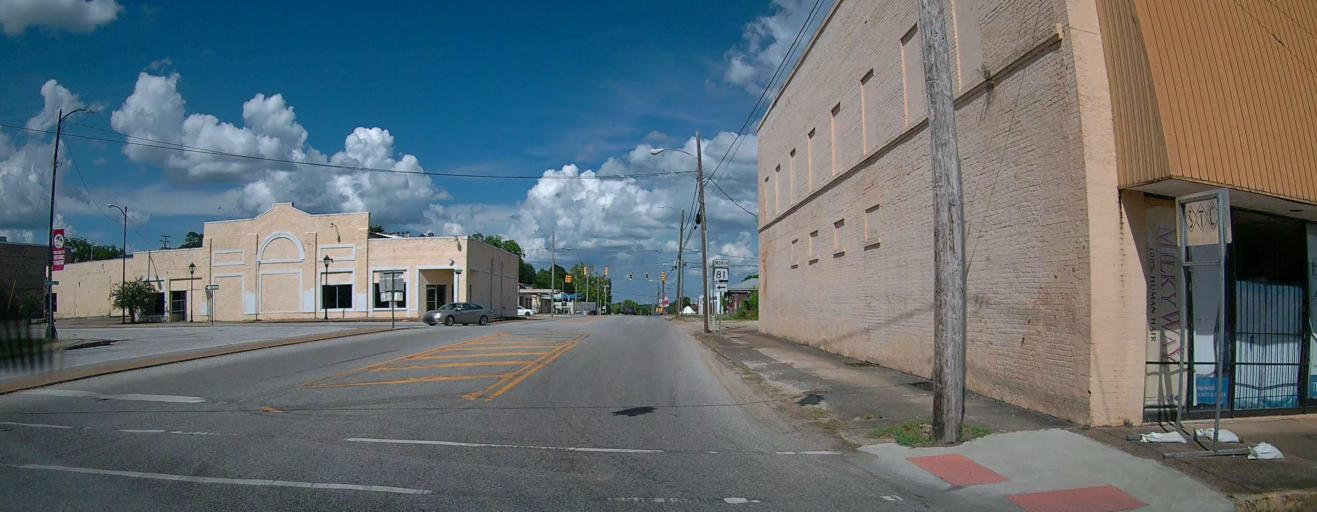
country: US
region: Alabama
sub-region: Macon County
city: Tuskegee
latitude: 32.4236
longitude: -85.6904
